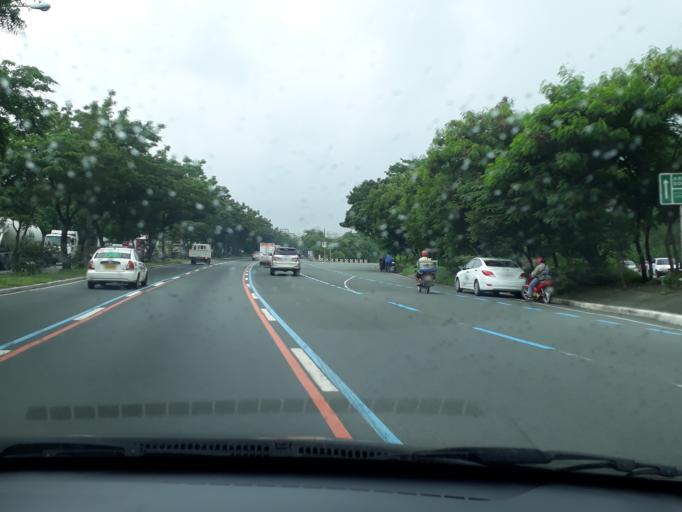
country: PH
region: Calabarzon
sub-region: Province of Rizal
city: Taguig
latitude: 14.5197
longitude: 121.0526
